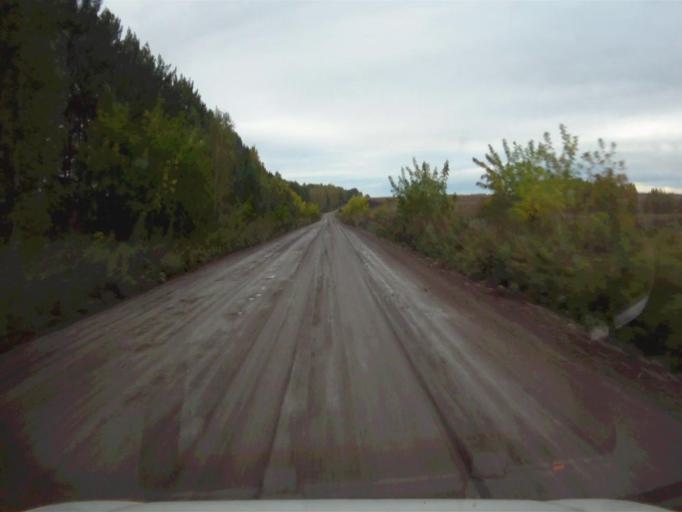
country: RU
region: Sverdlovsk
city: Mikhaylovsk
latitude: 56.1480
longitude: 59.2758
